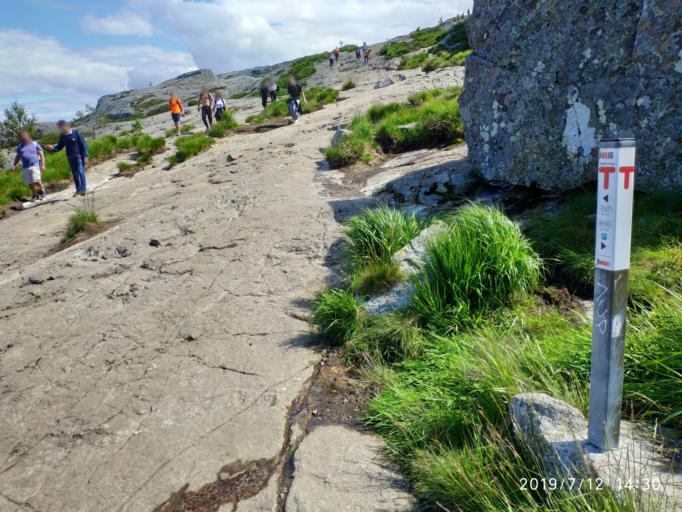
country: NO
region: Rogaland
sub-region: Forsand
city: Forsand
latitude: 58.9891
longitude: 6.1869
